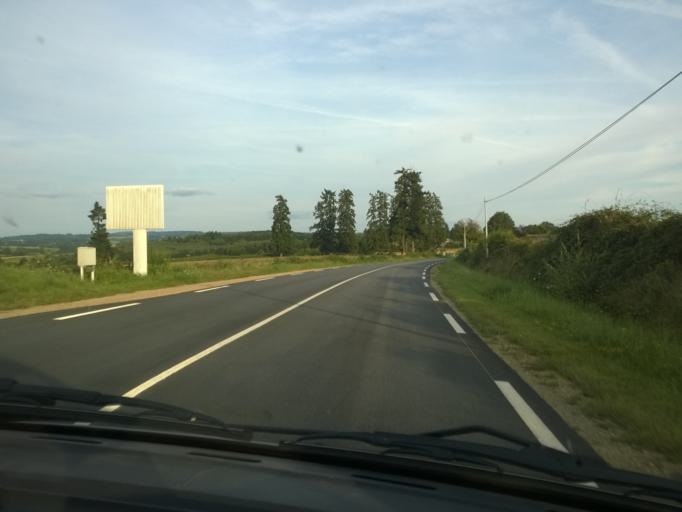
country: FR
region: Limousin
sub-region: Departement de la Haute-Vienne
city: Neuvic-Entier
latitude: 45.7585
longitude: 1.5898
